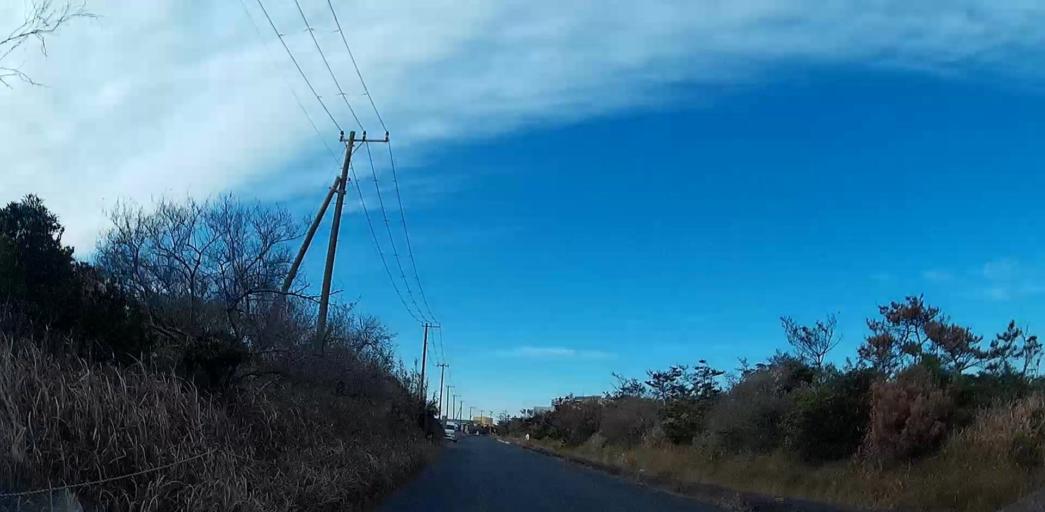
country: JP
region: Chiba
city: Hasaki
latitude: 35.7647
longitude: 140.8194
